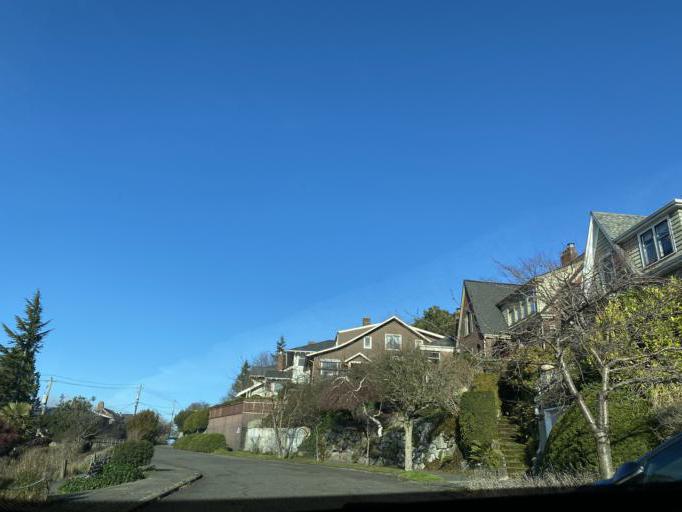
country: US
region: Washington
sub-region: King County
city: Seattle
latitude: 47.6408
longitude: -122.3713
